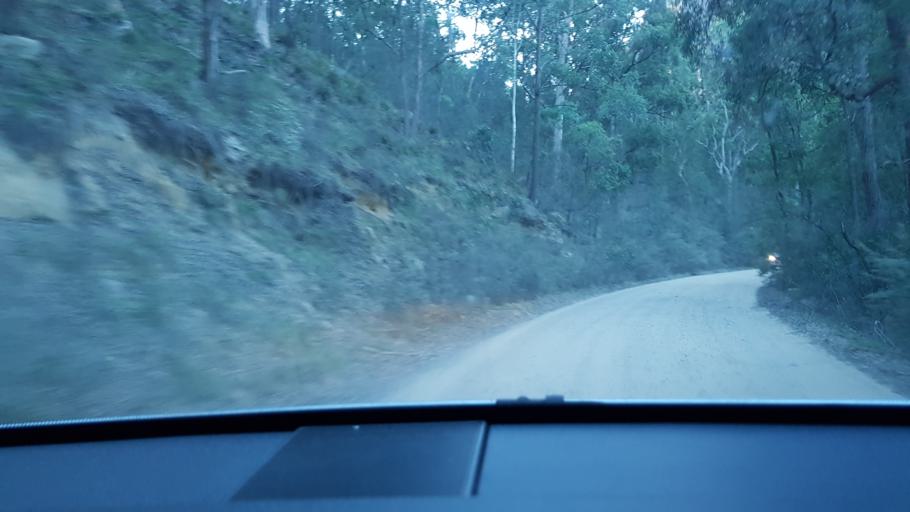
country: AU
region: New South Wales
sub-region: Lithgow
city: Portland
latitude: -33.1890
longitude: 150.2444
